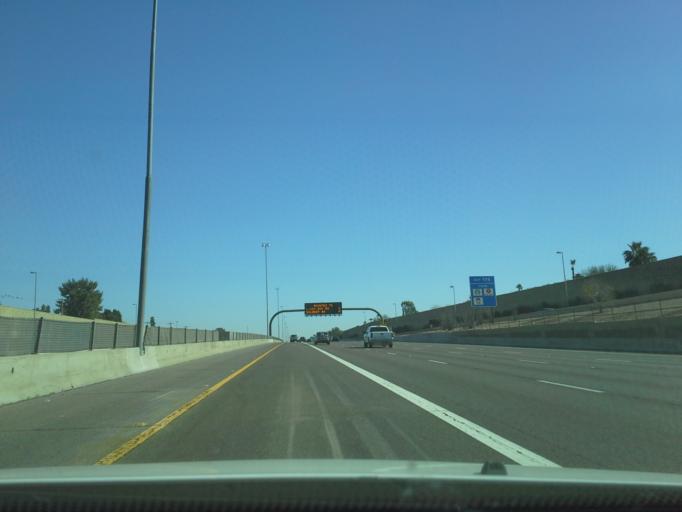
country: US
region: Arizona
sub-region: Maricopa County
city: Tempe
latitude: 33.3856
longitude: -111.9251
